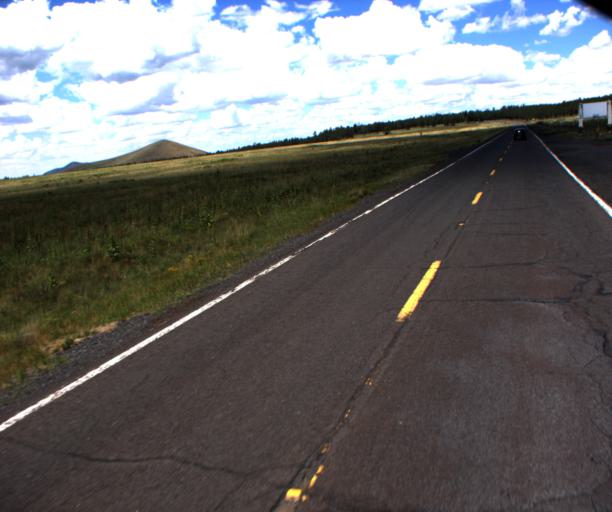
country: US
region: Arizona
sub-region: Coconino County
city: Flagstaff
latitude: 35.4127
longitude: -111.7556
